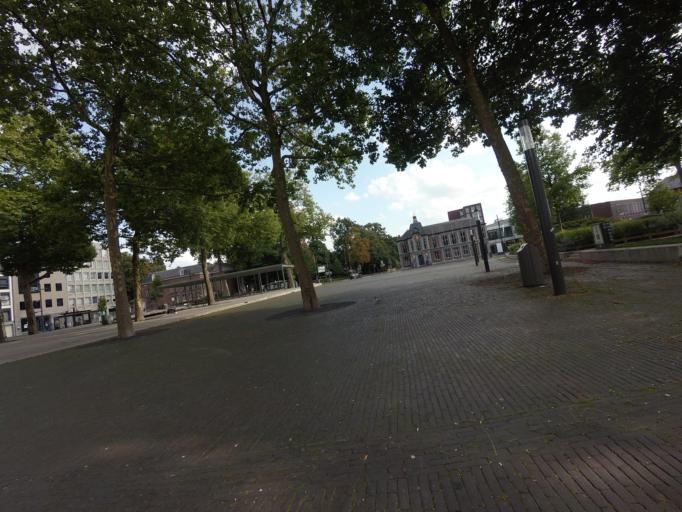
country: BE
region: Flanders
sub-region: Provincie Antwerpen
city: Aartselaar
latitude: 51.1704
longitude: 4.3942
